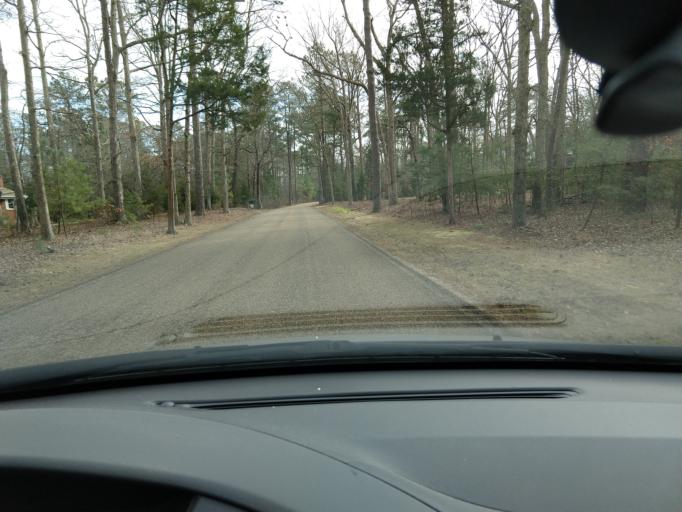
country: US
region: Virginia
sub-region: Chesterfield County
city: Bellwood
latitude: 37.4171
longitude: -77.3753
